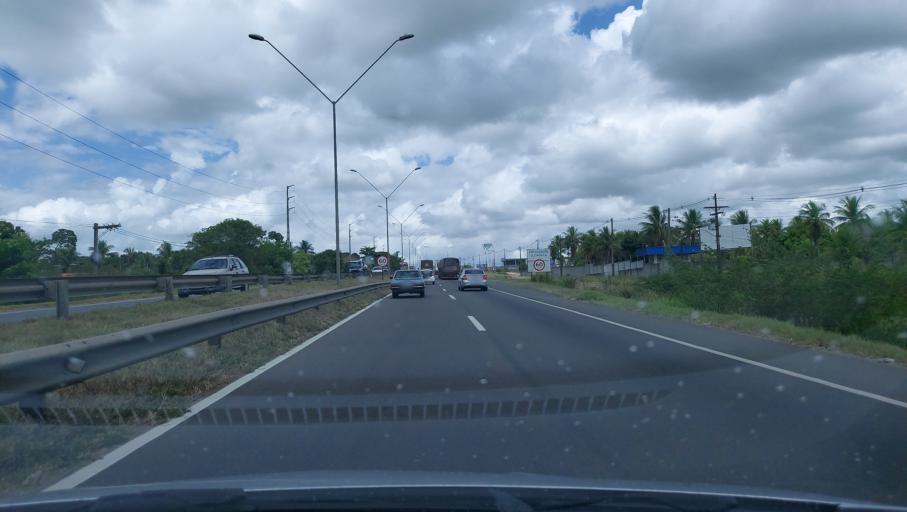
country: BR
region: Bahia
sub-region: Conceicao Do Jacuipe
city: Conceicao do Jacuipe
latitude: -12.3234
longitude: -38.8679
